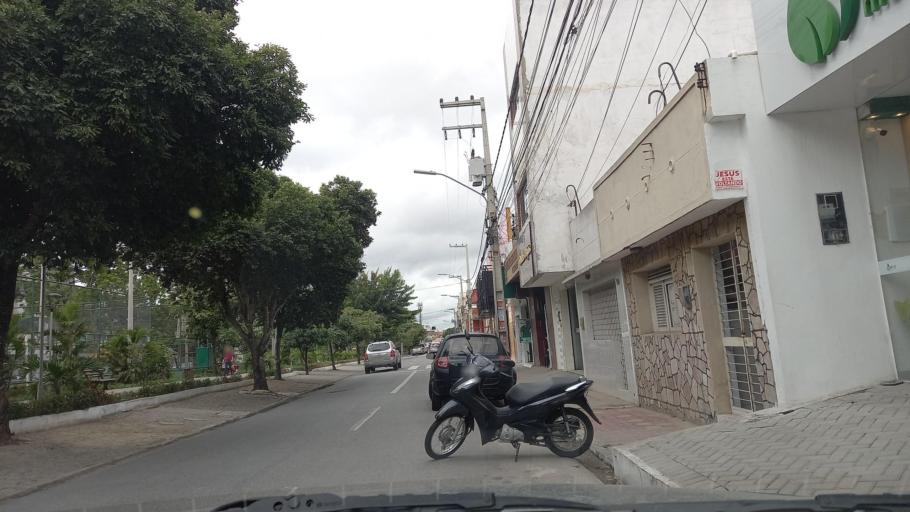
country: BR
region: Pernambuco
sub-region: Caruaru
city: Caruaru
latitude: -8.2794
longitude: -35.9751
